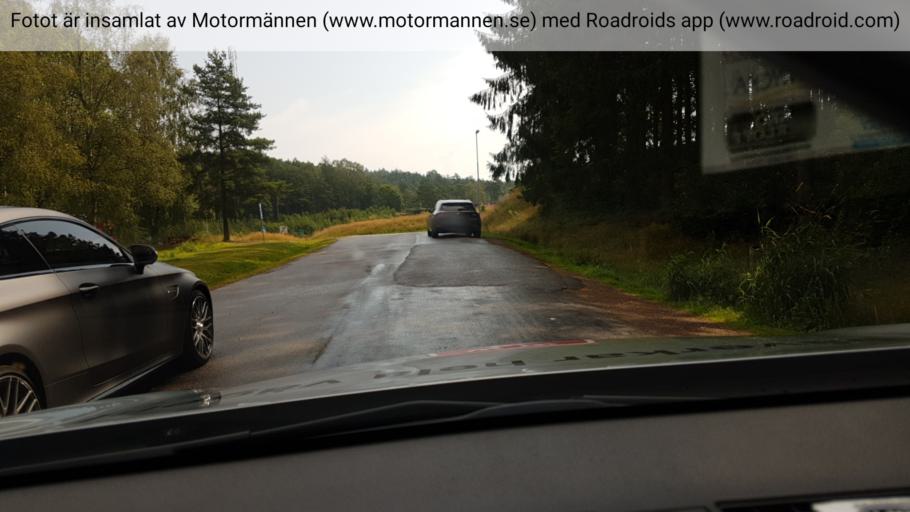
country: SE
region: Vaestra Goetaland
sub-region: Molndal
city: Lindome
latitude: 57.5540
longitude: 12.0503
